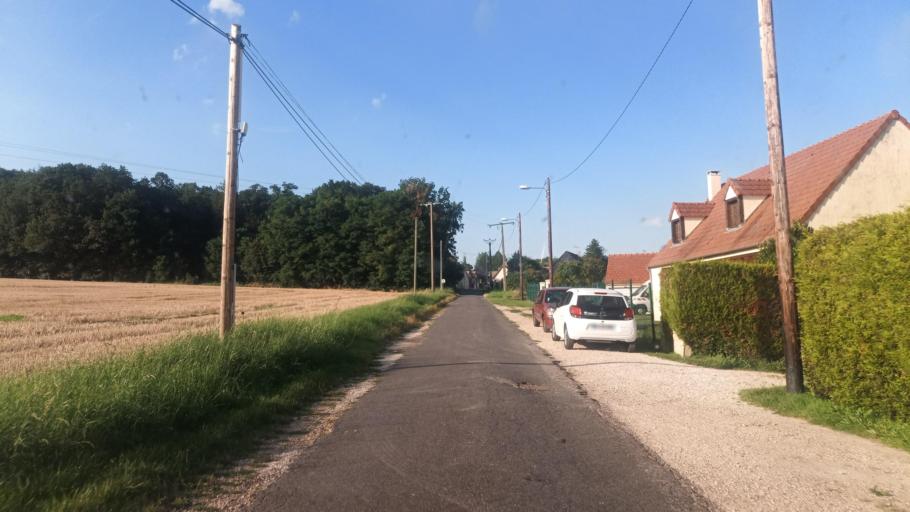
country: FR
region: Bourgogne
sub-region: Departement de l'Yonne
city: Pont-sur-Yonne
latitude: 48.2663
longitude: 3.1845
